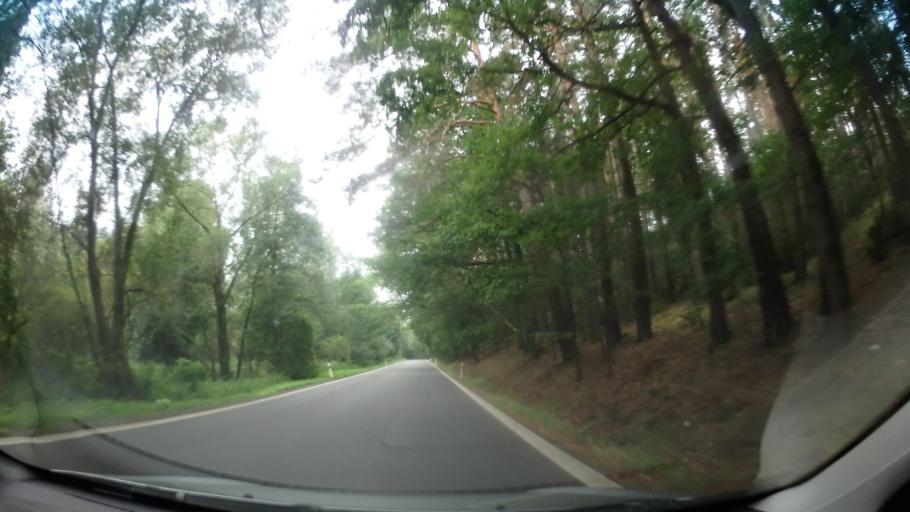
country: CZ
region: Central Bohemia
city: Bystrice
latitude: 49.7599
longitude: 14.6350
